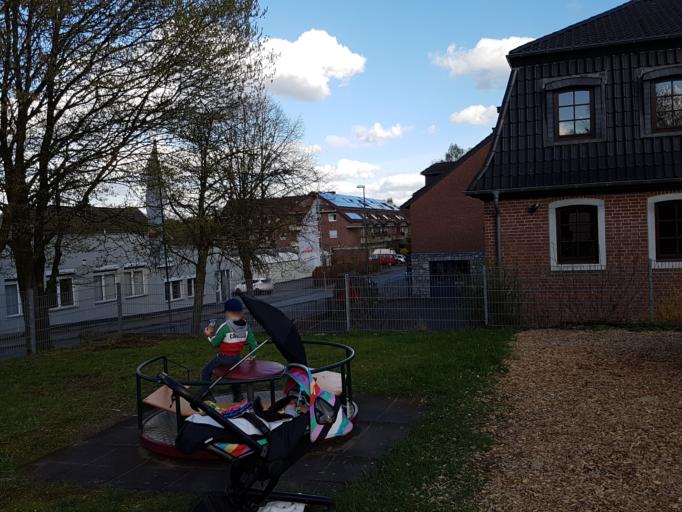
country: DE
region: North Rhine-Westphalia
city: Stolberg
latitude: 50.7315
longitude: 6.1704
